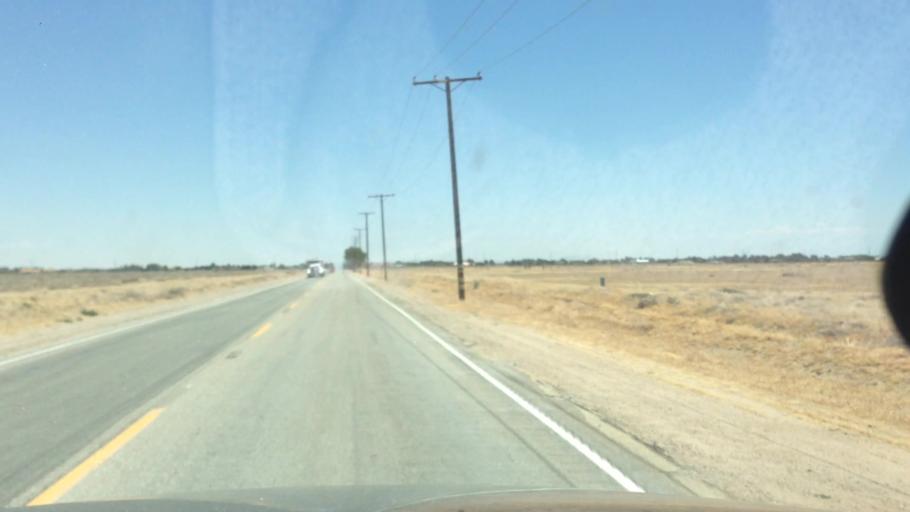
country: US
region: California
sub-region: Los Angeles County
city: Quartz Hill
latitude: 34.7764
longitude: -118.3030
